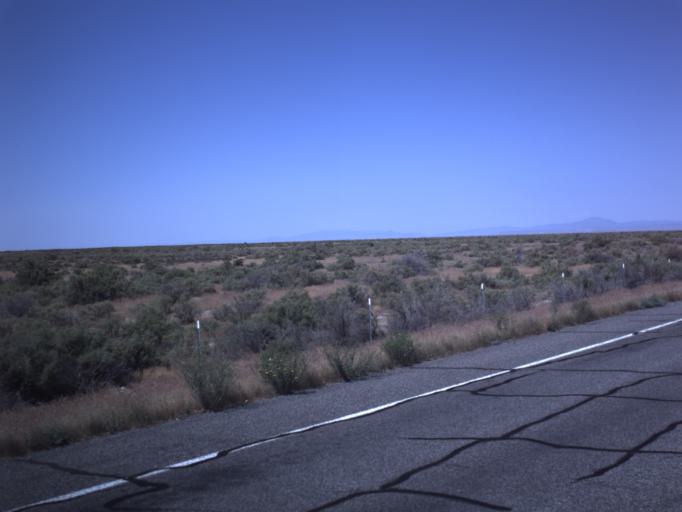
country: US
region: Utah
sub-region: Millard County
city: Delta
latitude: 39.4696
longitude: -112.4575
